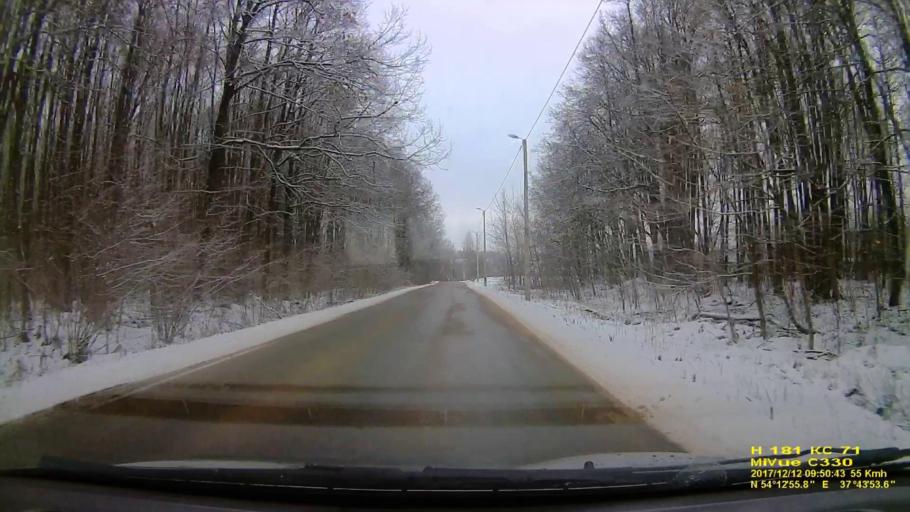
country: RU
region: Tula
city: Tula
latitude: 54.2155
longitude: 37.7322
